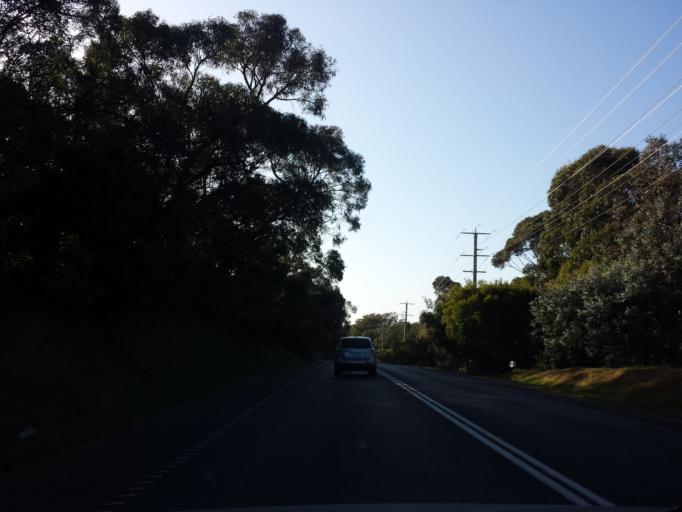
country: AU
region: Victoria
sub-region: Yarra Ranges
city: Belgrave South
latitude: -37.9583
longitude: 145.3542
